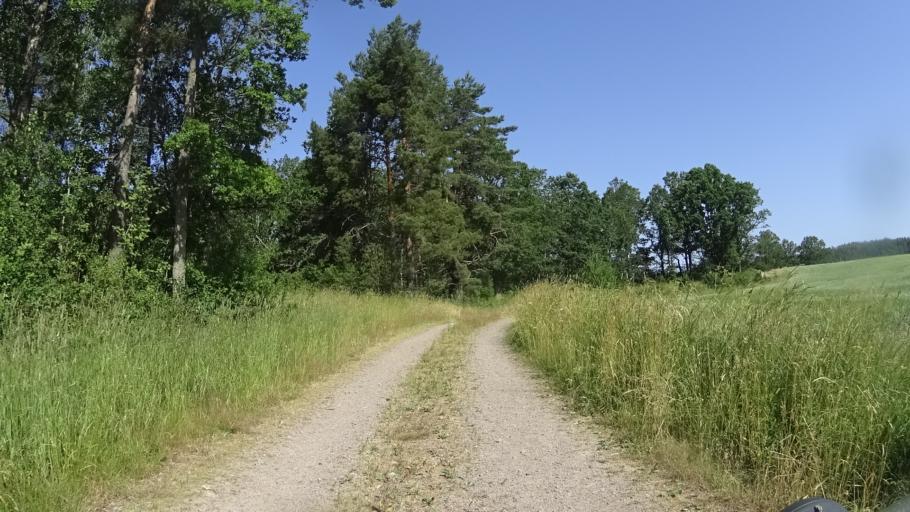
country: SE
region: Kalmar
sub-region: Vasterviks Kommun
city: Gamleby
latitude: 57.9241
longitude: 16.3997
